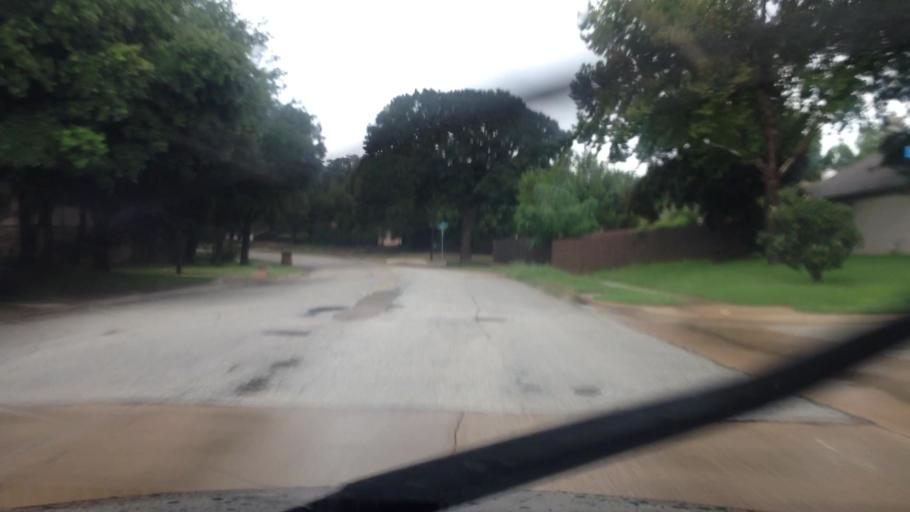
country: US
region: Texas
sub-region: Tarrant County
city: Watauga
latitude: 32.8821
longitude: -97.2094
